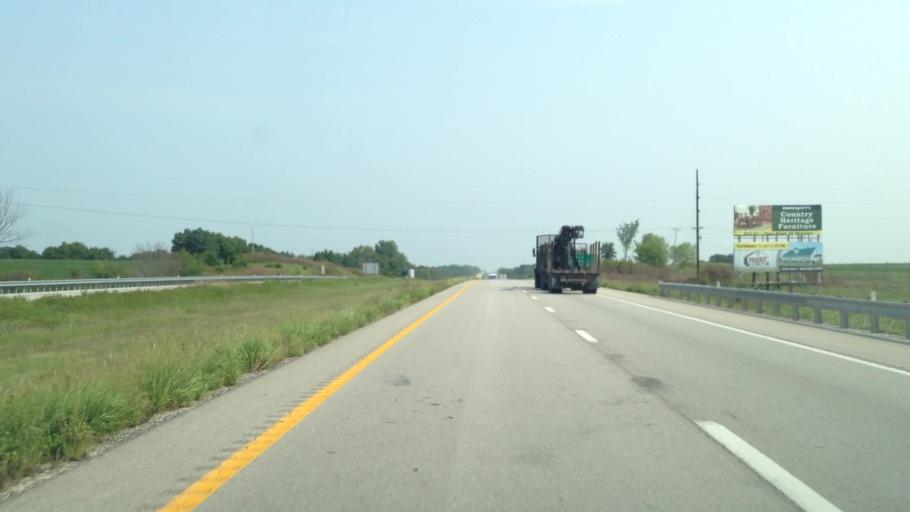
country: US
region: Missouri
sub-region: Clinton County
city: Cameron
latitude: 39.7631
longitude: -94.2168
